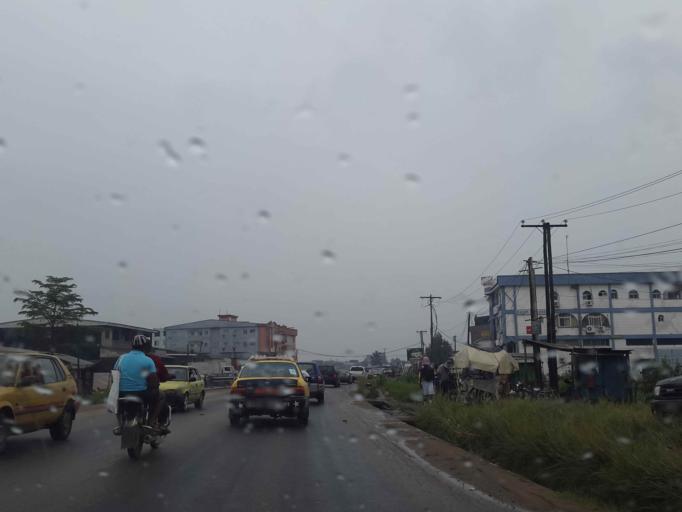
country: CM
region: Littoral
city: Douala
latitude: 4.0830
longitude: 9.7314
